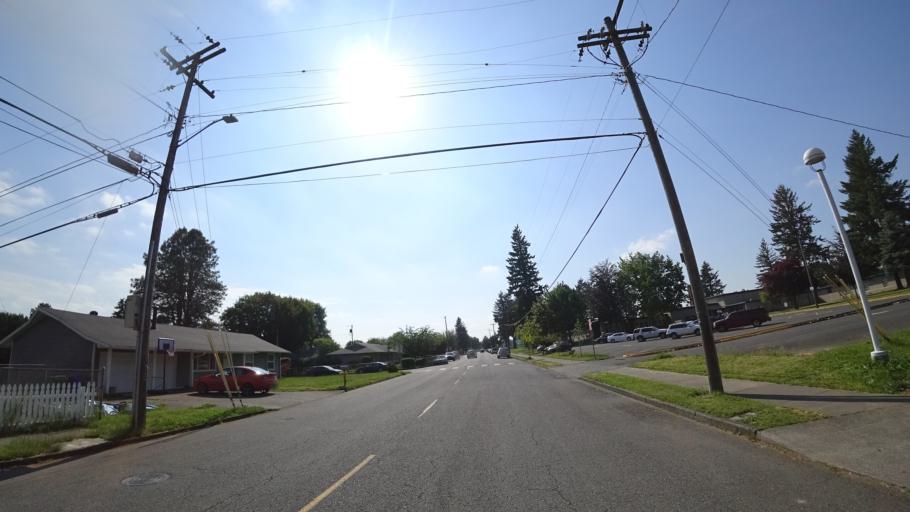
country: US
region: Oregon
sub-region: Multnomah County
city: Gresham
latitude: 45.5138
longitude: -122.4990
